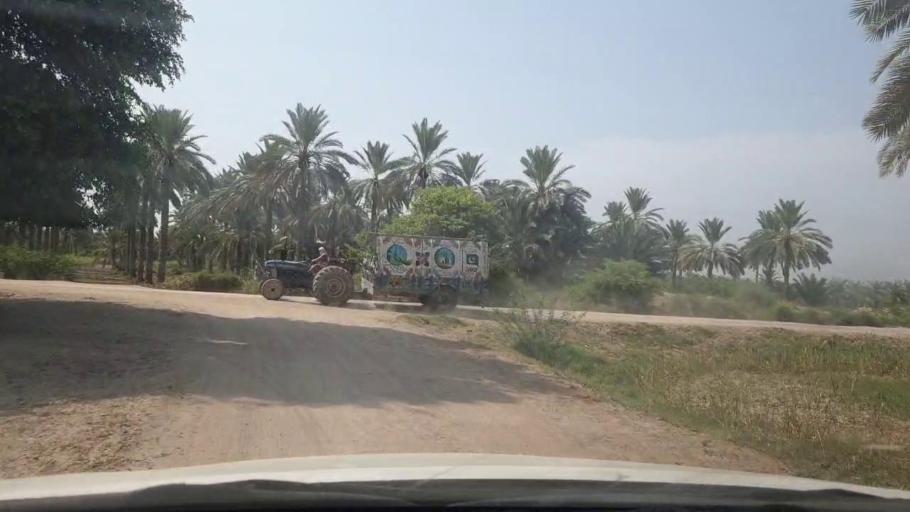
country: PK
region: Sindh
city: Rohri
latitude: 27.5942
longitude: 68.8505
